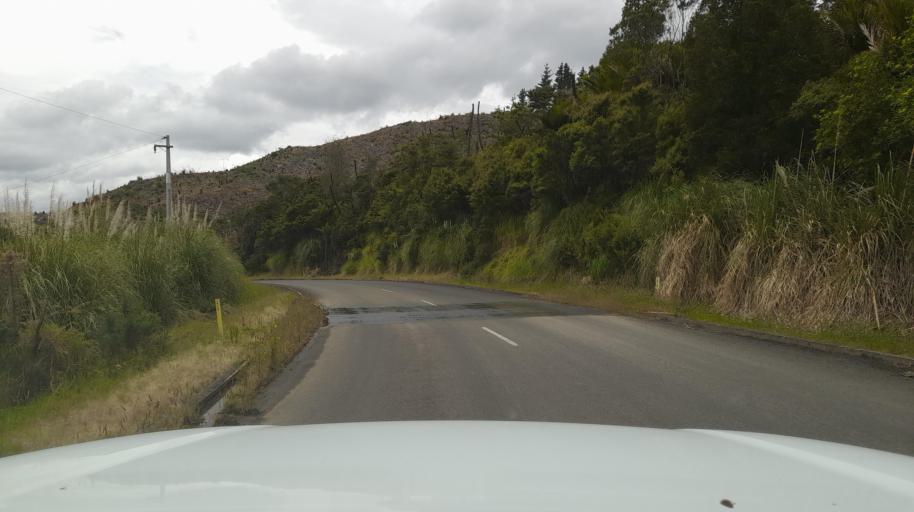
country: NZ
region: Northland
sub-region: Far North District
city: Kaitaia
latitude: -35.3711
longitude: 173.4325
